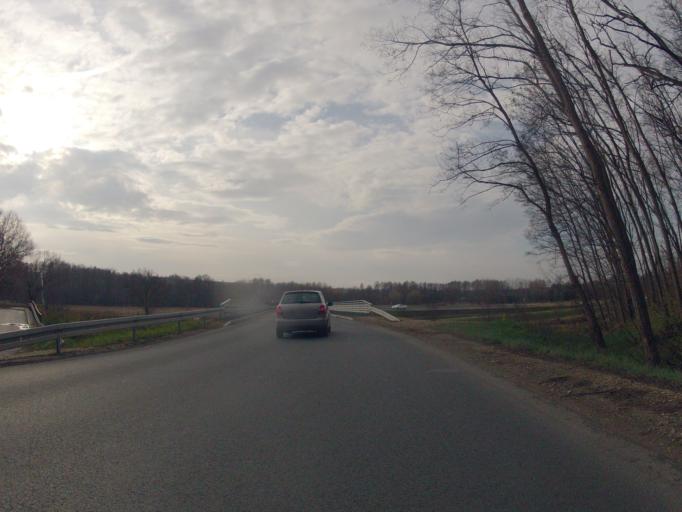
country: PL
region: Lesser Poland Voivodeship
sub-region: Powiat krakowski
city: Balice
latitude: 50.0870
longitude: 19.8165
